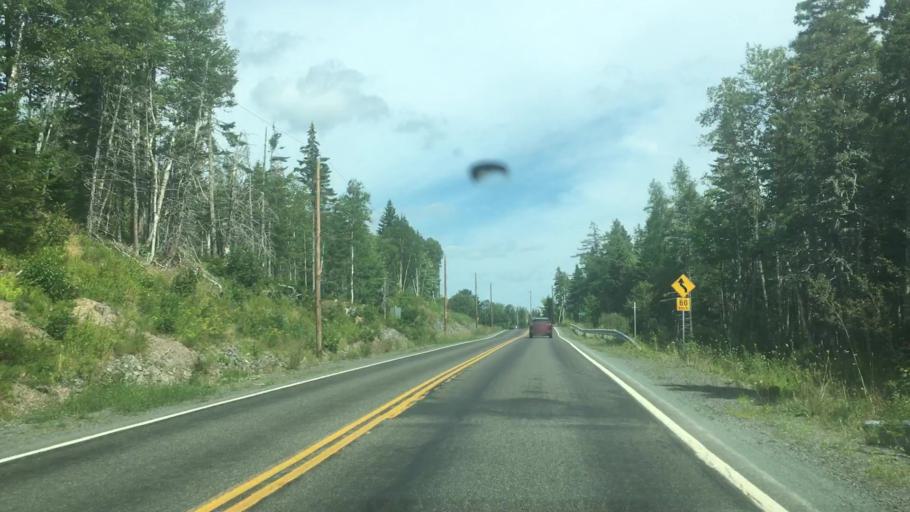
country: CA
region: Nova Scotia
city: Sydney Mines
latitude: 46.2107
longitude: -60.6210
